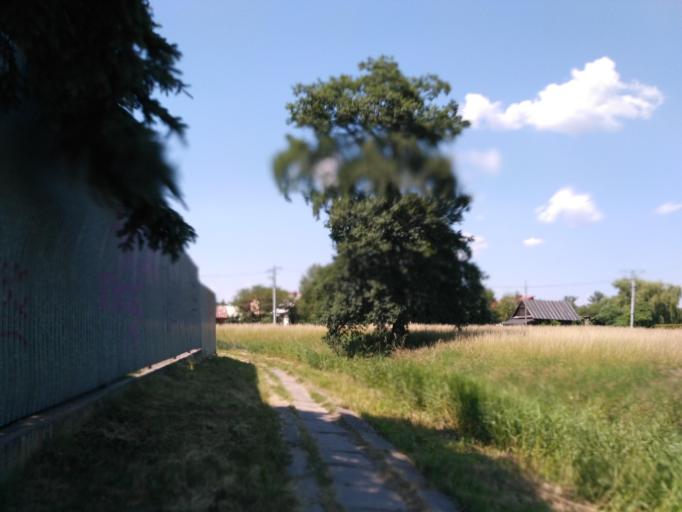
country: PL
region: Subcarpathian Voivodeship
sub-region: Powiat brzozowski
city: Brzozow
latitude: 49.6994
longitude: 22.0242
